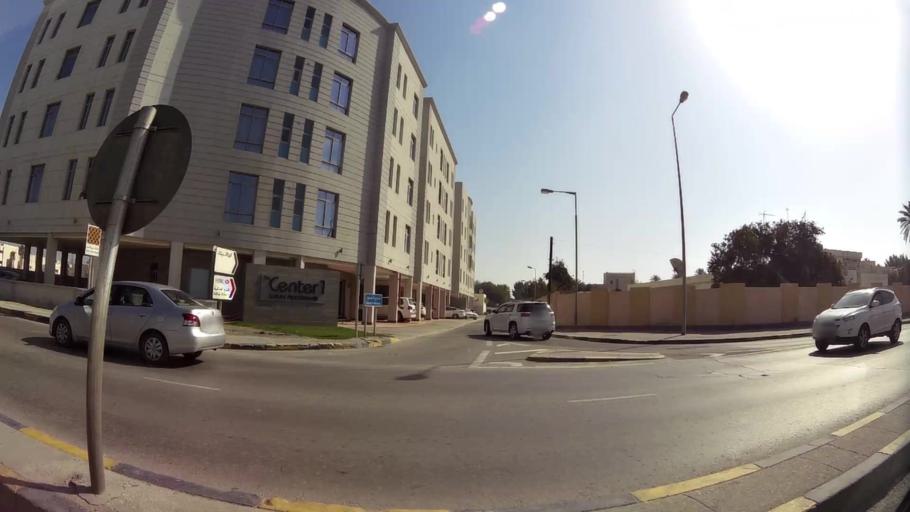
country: BH
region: Manama
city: Manama
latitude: 26.2183
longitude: 50.5794
